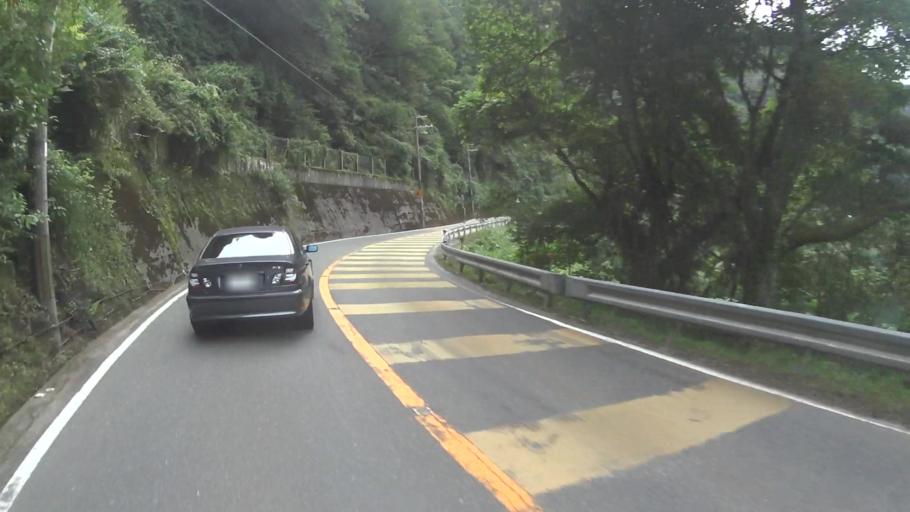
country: JP
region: Kyoto
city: Uji
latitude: 34.8699
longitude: 135.8362
